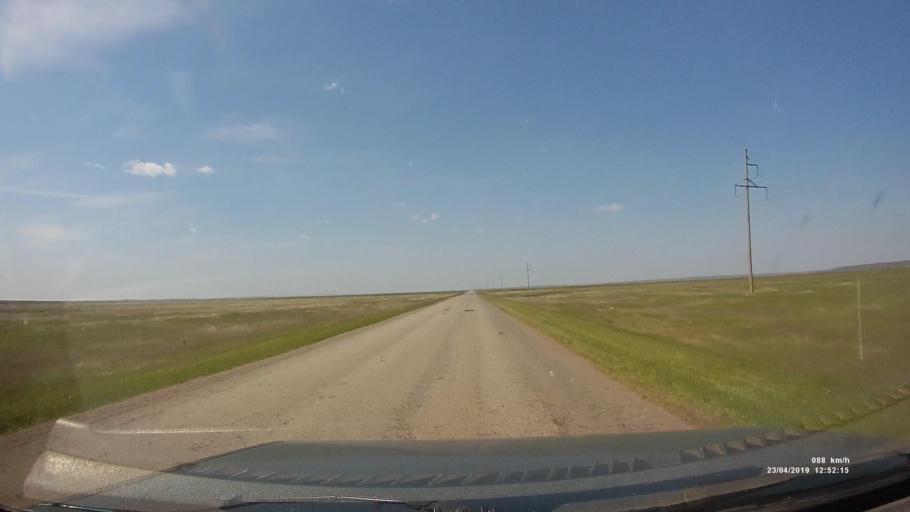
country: RU
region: Kalmykiya
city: Yashalta
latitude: 46.5629
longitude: 42.6119
